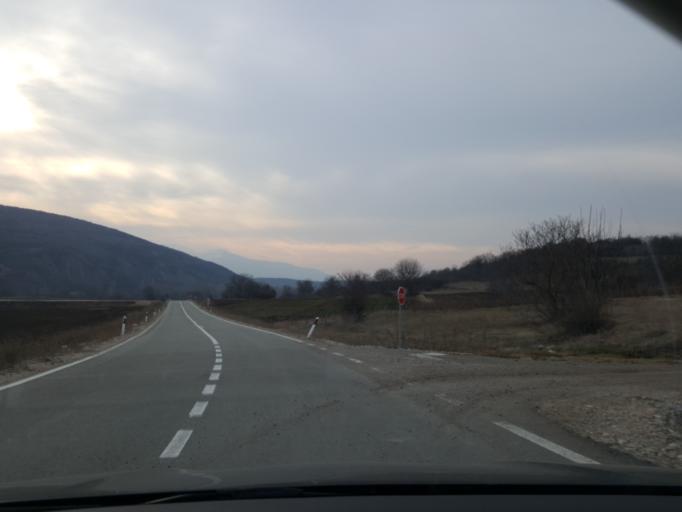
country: RS
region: Central Serbia
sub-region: Pirotski Okrug
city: Pirot
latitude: 43.2275
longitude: 22.4758
